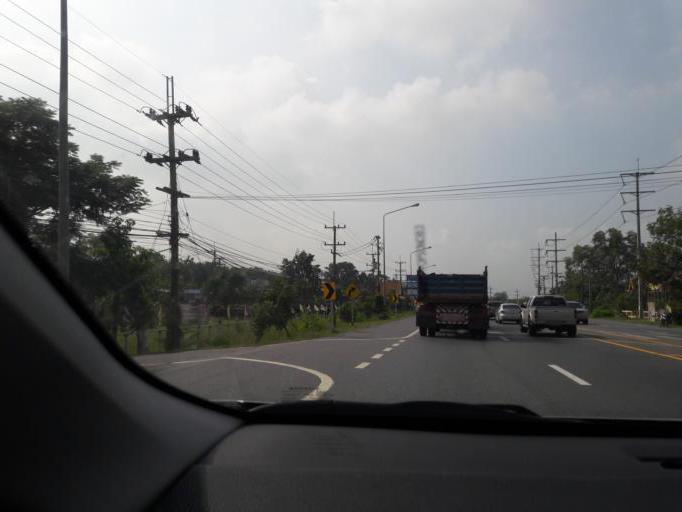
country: TH
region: Ang Thong
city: Ang Thong
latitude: 14.5701
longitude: 100.4541
